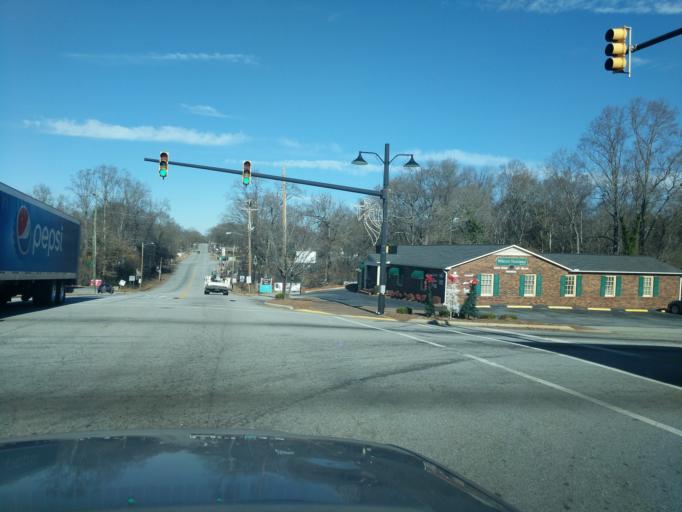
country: US
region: South Carolina
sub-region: Spartanburg County
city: Mayo
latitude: 35.1485
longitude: -81.8603
